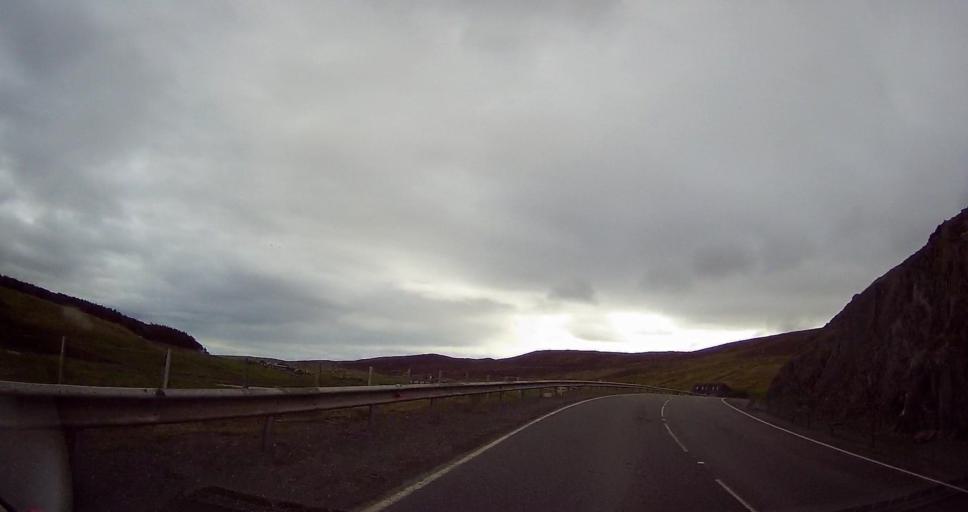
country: GB
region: Scotland
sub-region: Shetland Islands
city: Lerwick
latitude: 60.4085
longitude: -1.3340
